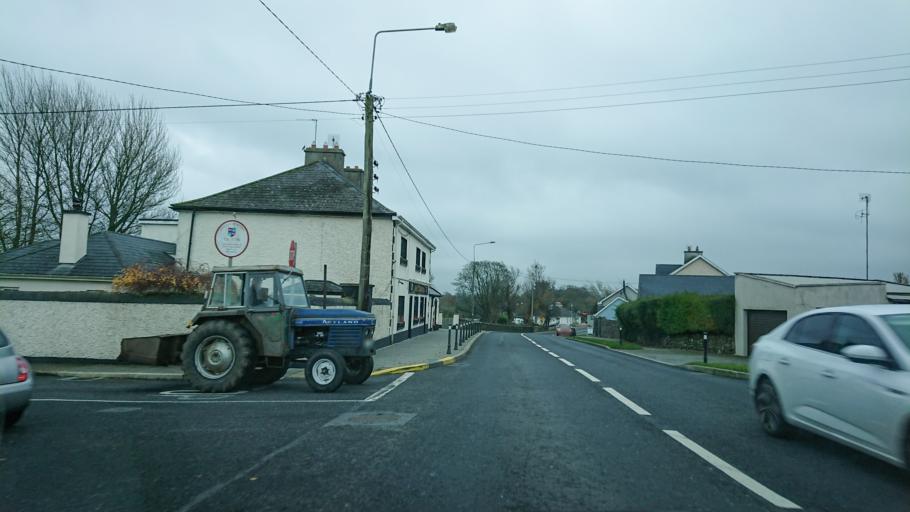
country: IE
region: Leinster
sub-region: Kilkenny
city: Mooncoin
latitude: 52.2957
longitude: -7.2596
